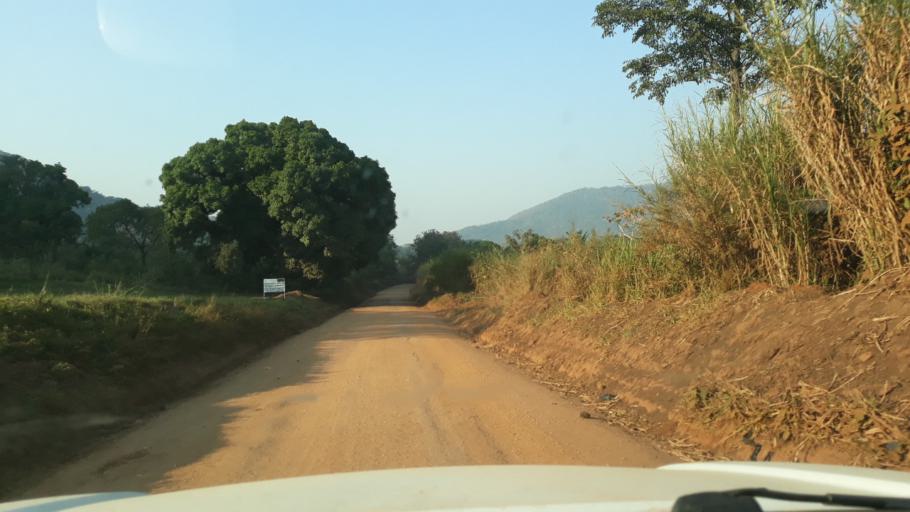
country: BI
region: Bururi
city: Rumonge
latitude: -4.2878
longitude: 28.9586
